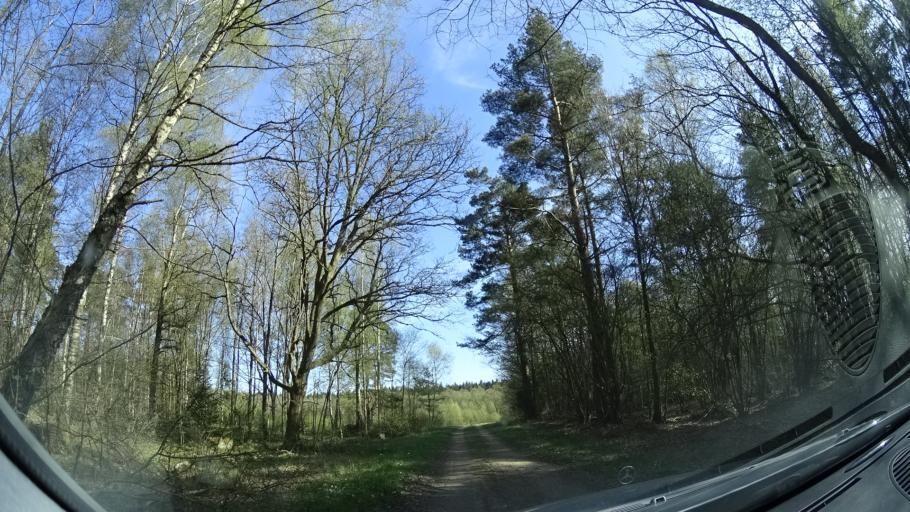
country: SE
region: Skane
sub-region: Hassleholms Kommun
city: Tormestorp
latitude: 56.1002
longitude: 13.6708
